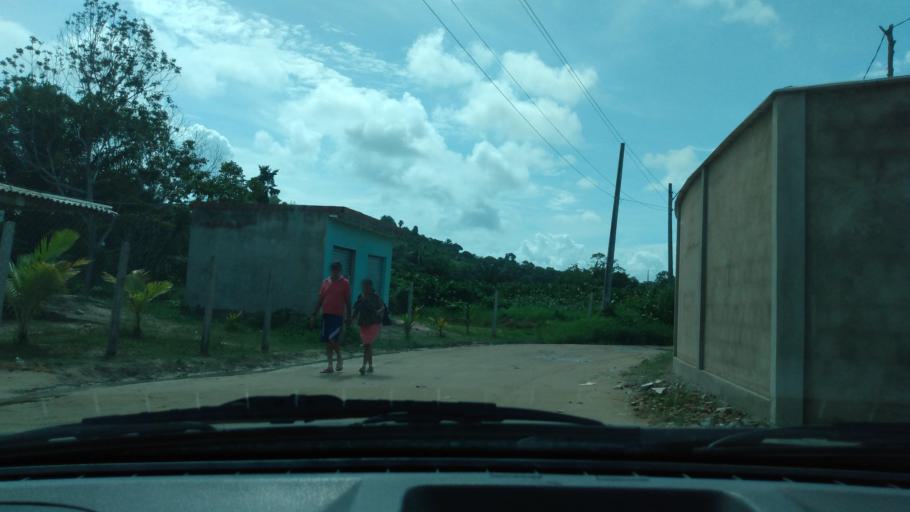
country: BR
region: Pernambuco
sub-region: Cabo De Santo Agostinho
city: Cabo
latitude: -8.3460
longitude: -34.9644
